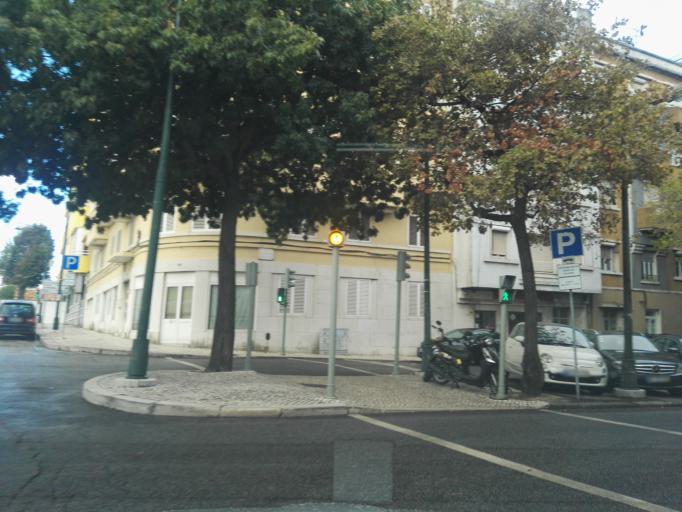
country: PT
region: Lisbon
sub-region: Lisbon
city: Lisbon
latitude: 38.7279
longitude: -9.1594
